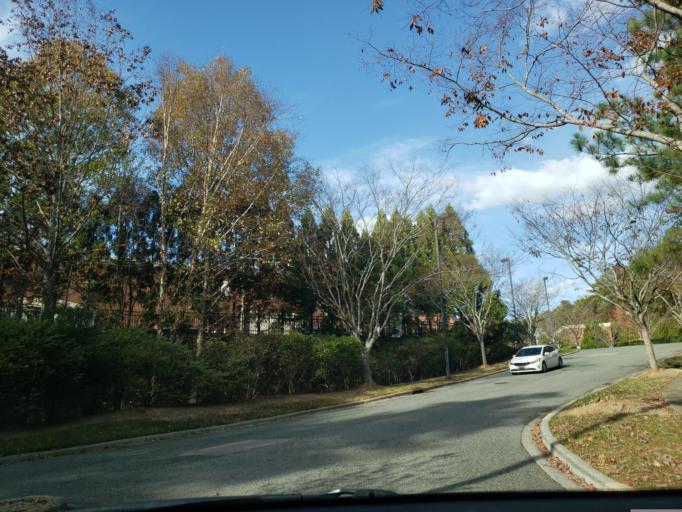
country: US
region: North Carolina
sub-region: Wake County
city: Green Level
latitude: 35.7844
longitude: -78.8700
